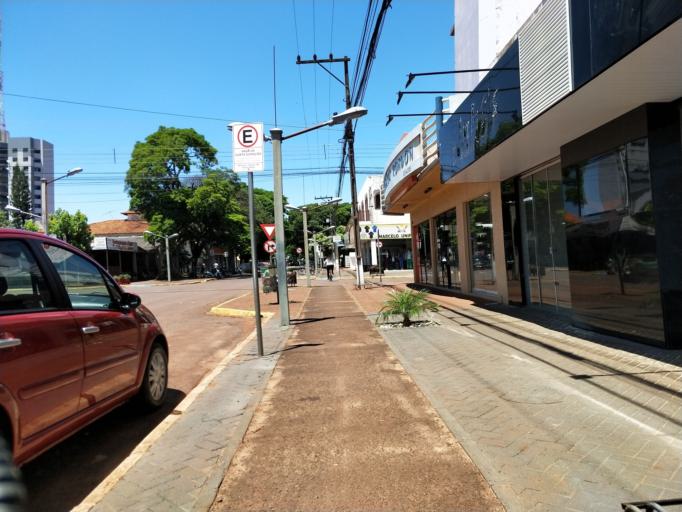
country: BR
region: Parana
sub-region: Marechal Candido Rondon
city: Marechal Candido Rondon
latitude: -24.5600
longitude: -54.0604
